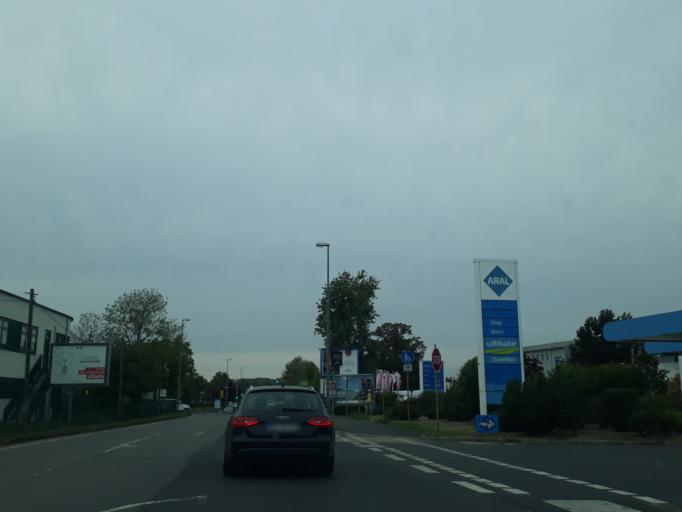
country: DE
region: Saxony
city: Radebeul
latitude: 51.0902
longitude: 13.6754
